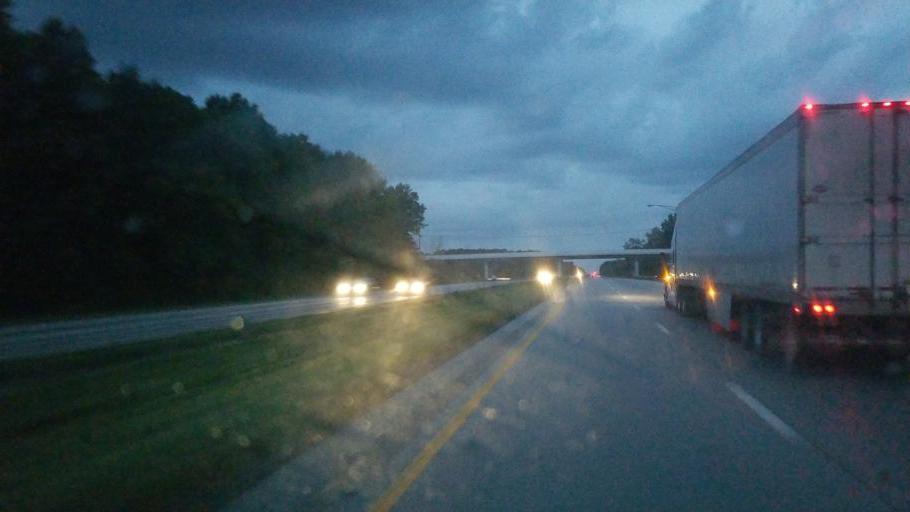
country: US
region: Ohio
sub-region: Medina County
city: Seville
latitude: 41.0320
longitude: -81.8078
